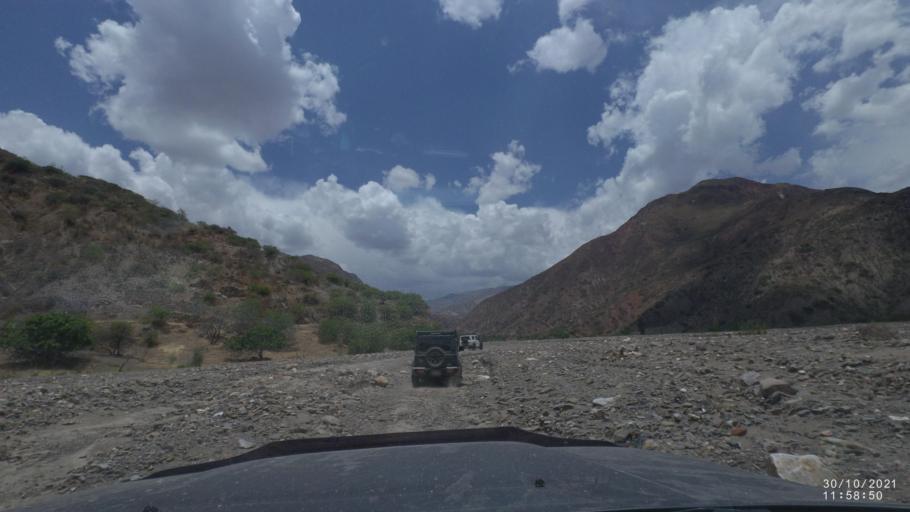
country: BO
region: Cochabamba
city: Colchani
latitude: -17.5246
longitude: -66.6181
